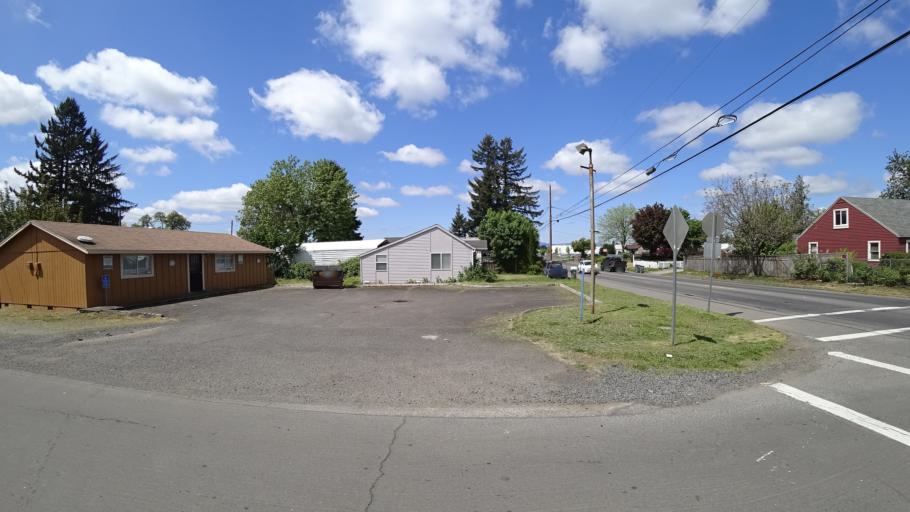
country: US
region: Oregon
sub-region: Washington County
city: Hillsboro
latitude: 45.5175
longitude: -122.9958
